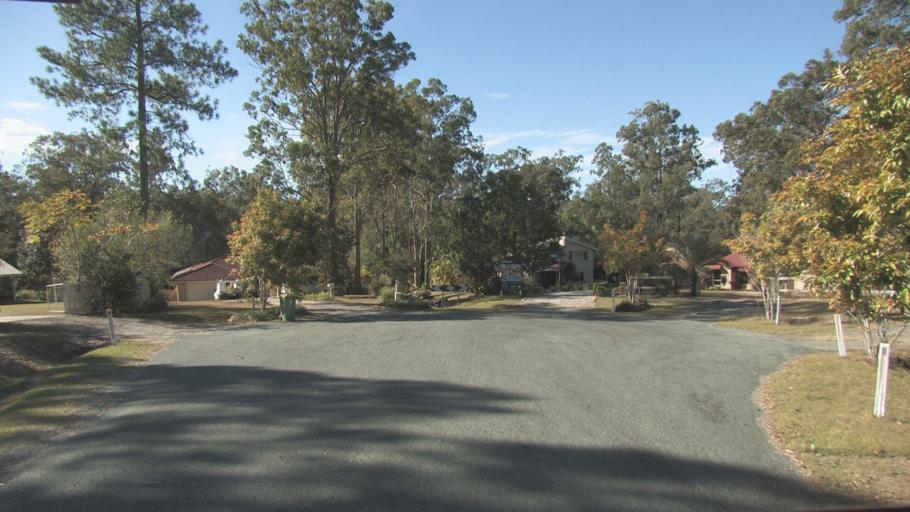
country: AU
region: Queensland
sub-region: Ipswich
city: Springfield Lakes
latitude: -27.7281
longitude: 152.9263
